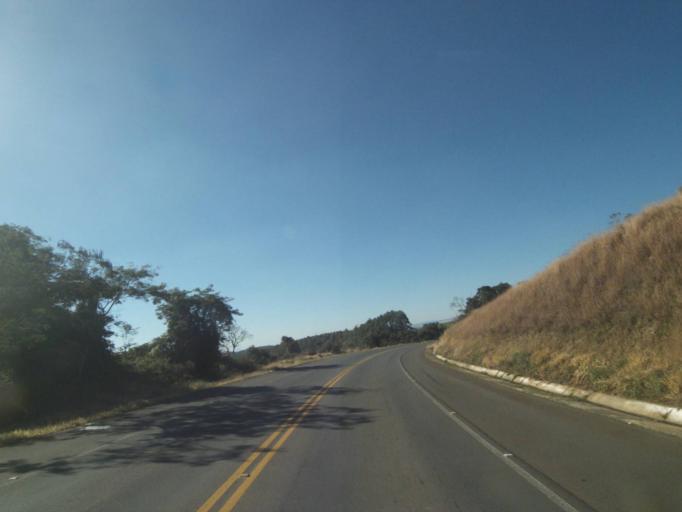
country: BR
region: Parana
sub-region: Tibagi
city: Tibagi
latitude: -24.7555
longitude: -50.4691
